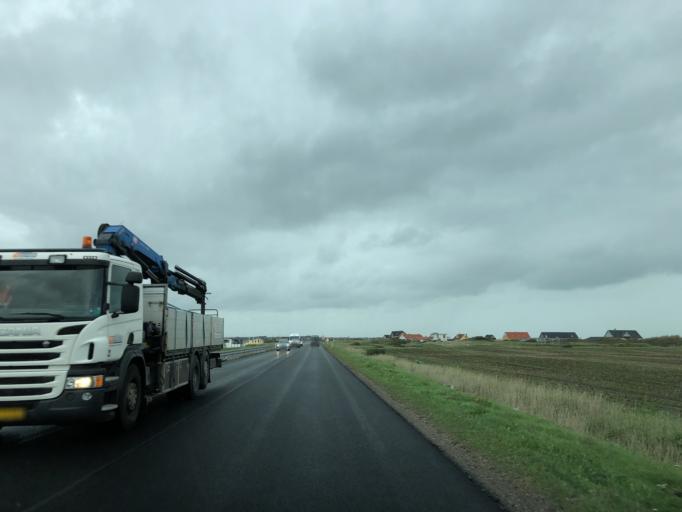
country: DK
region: Central Jutland
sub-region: Struer Kommune
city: Struer
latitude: 56.5689
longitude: 8.5611
